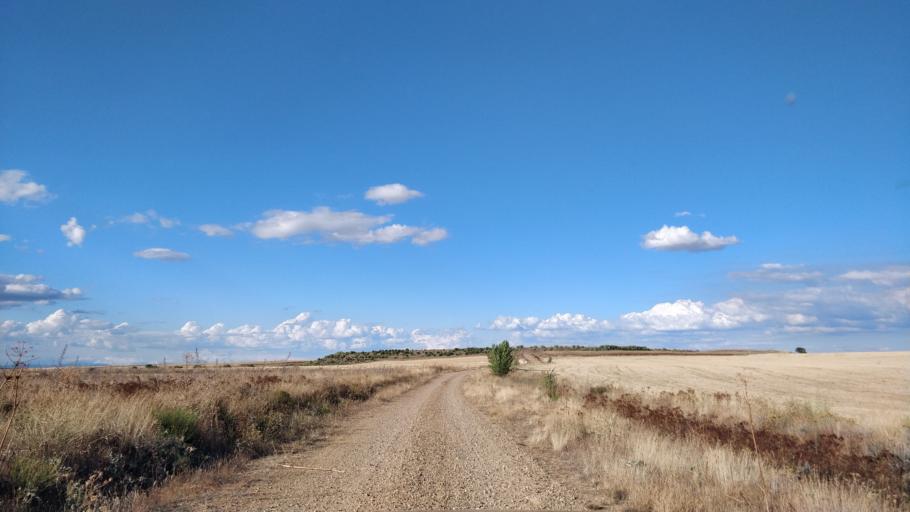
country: ES
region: Castille and Leon
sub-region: Provincia de Leon
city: Santa Cristina de Valmadrigal
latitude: 42.3415
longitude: -5.2713
